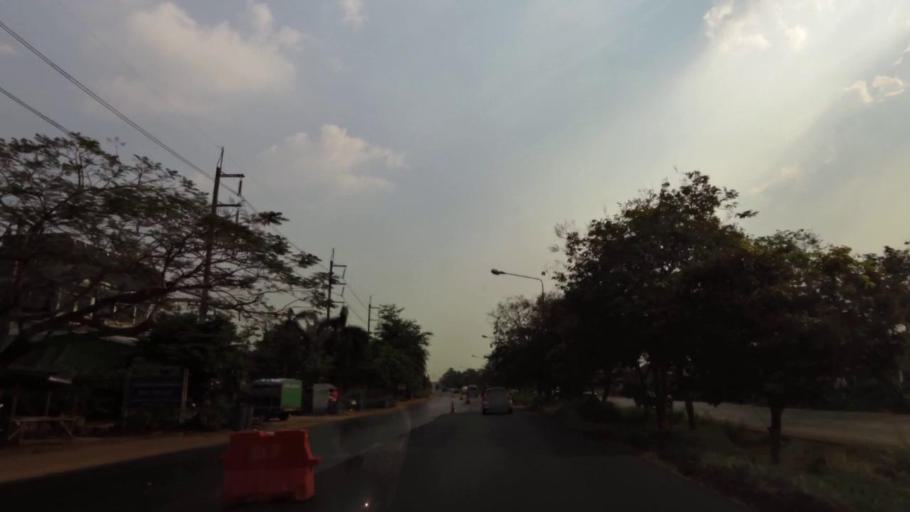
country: TH
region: Rayong
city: Klaeng
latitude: 12.8268
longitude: 101.6287
